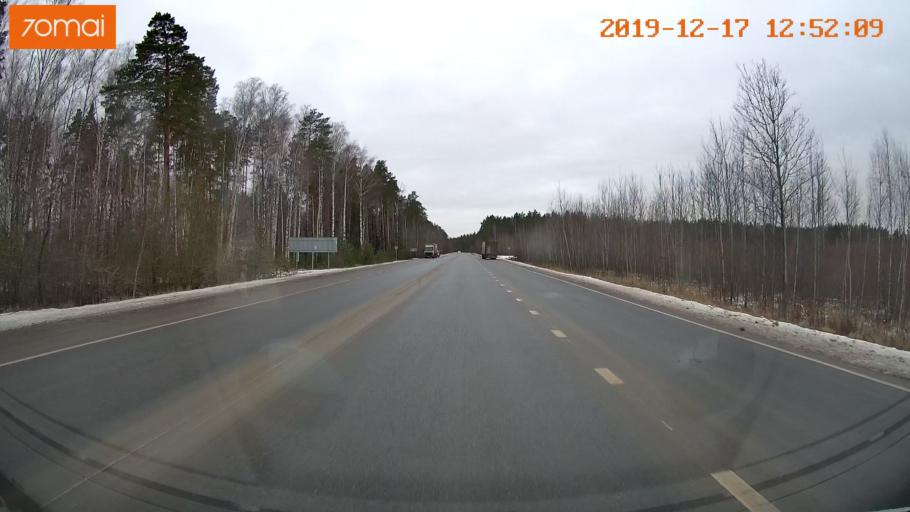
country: RU
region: Rjazan
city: Solotcha
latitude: 54.8559
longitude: 39.9602
